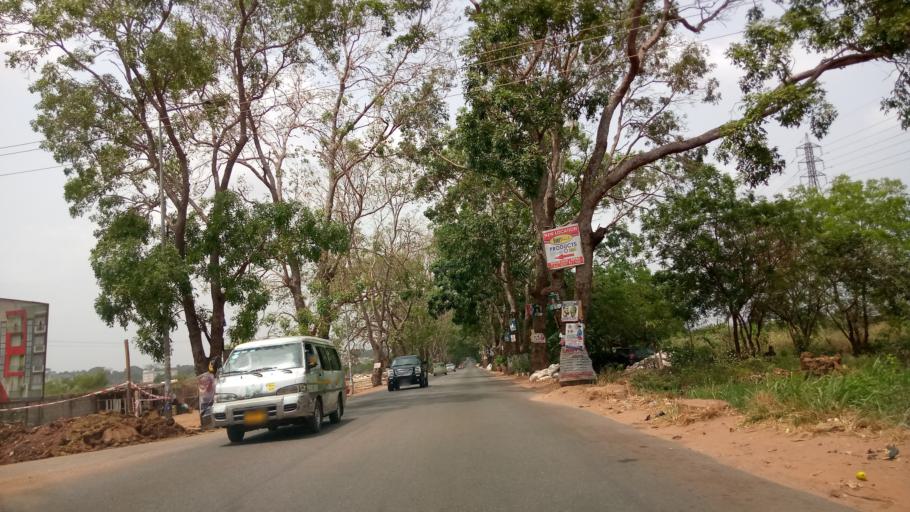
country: GH
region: Greater Accra
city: Dome
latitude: 5.6676
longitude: -0.2209
